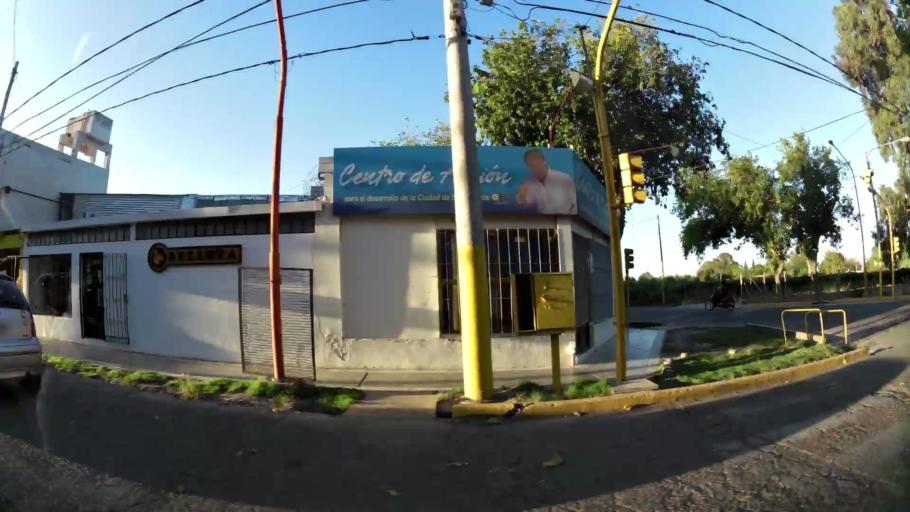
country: AR
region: San Juan
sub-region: Departamento de Santa Lucia
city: Santa Lucia
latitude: -31.5334
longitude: -68.4941
